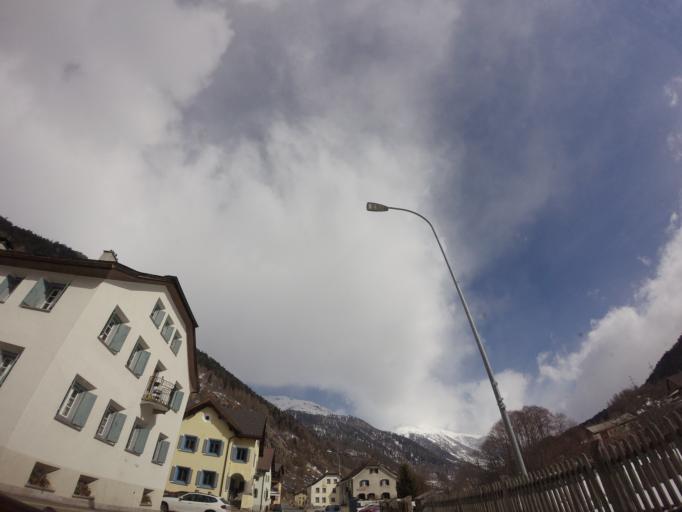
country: CH
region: Grisons
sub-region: Inn District
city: Zernez
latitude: 46.7513
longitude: 10.0808
